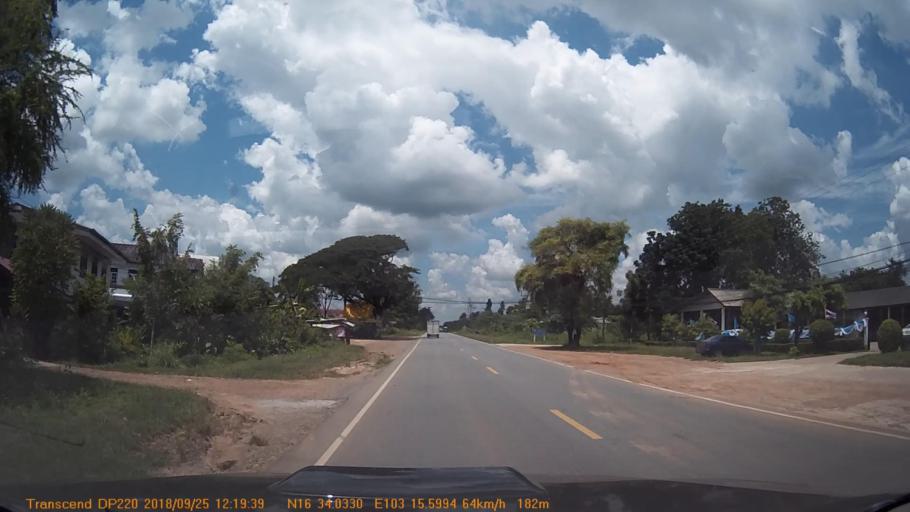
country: TH
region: Kalasin
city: Huai Mek
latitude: 16.5672
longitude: 103.2600
